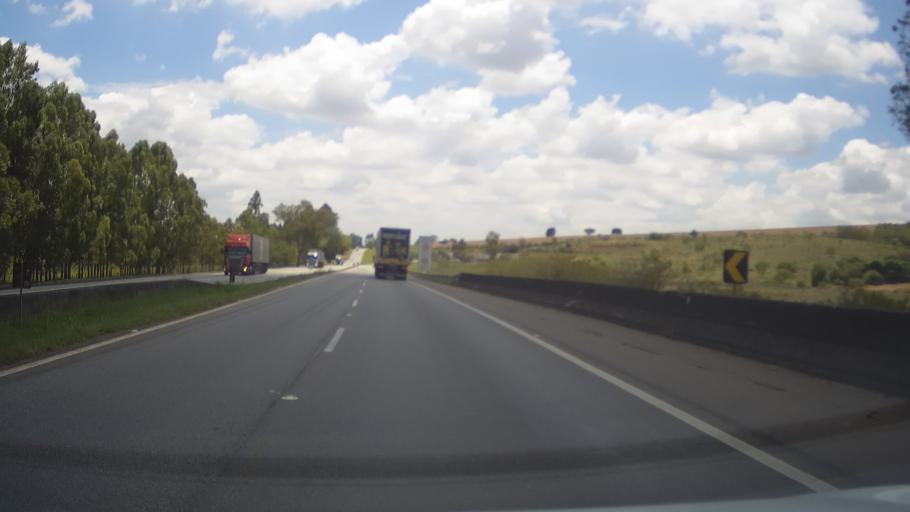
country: BR
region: Minas Gerais
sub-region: Campanha
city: Campanha
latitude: -21.7964
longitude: -45.4548
